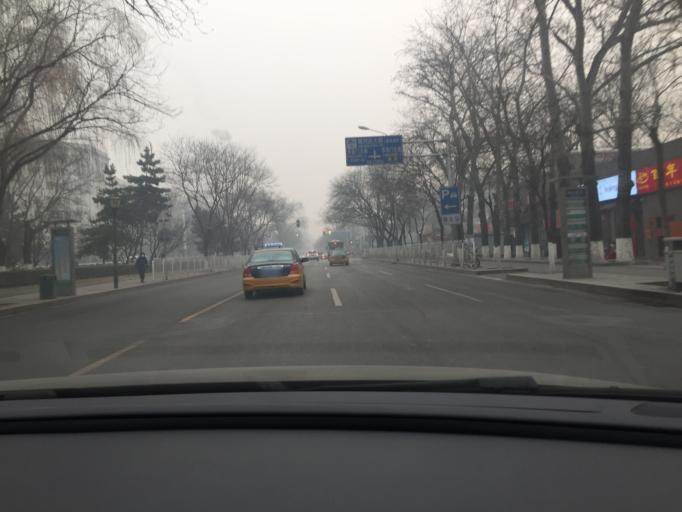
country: CN
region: Beijing
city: Beijing
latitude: 39.9149
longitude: 116.4003
